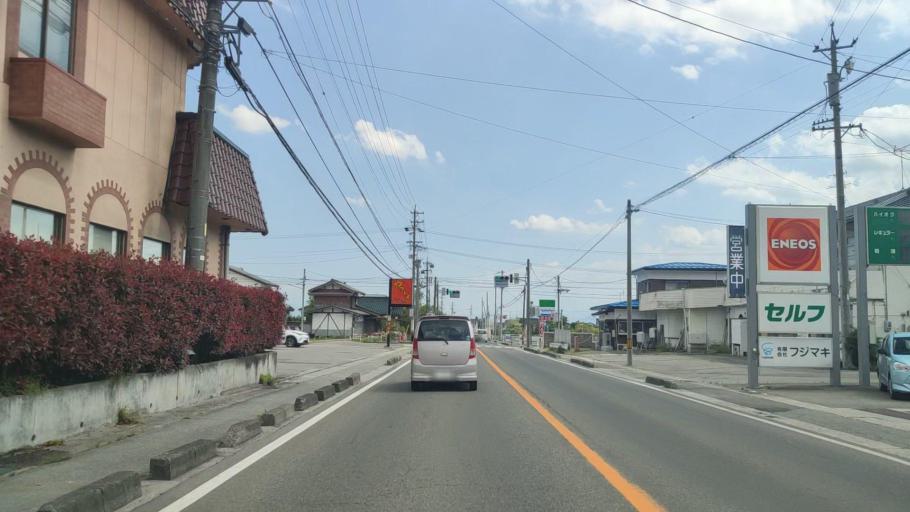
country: JP
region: Nagano
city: Omachi
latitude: 36.4691
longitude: 137.8490
